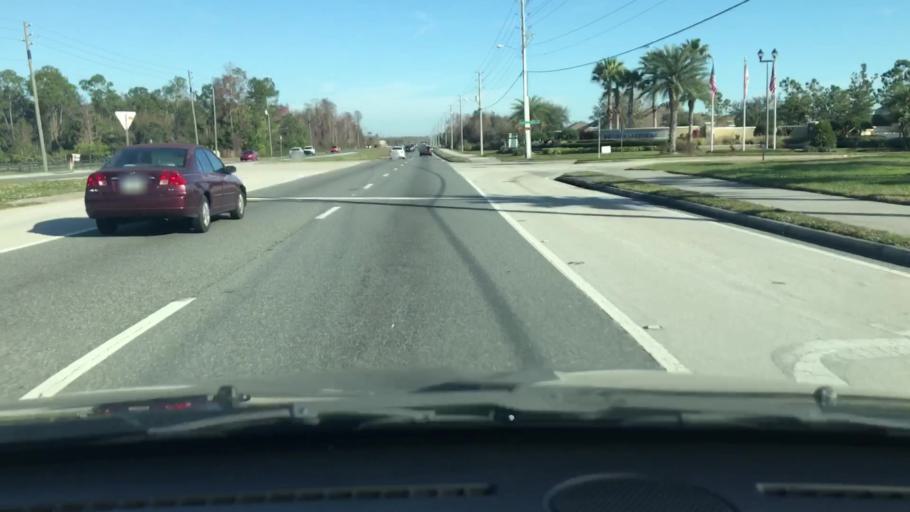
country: US
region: Florida
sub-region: Osceola County
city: Campbell
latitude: 28.2056
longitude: -81.4399
